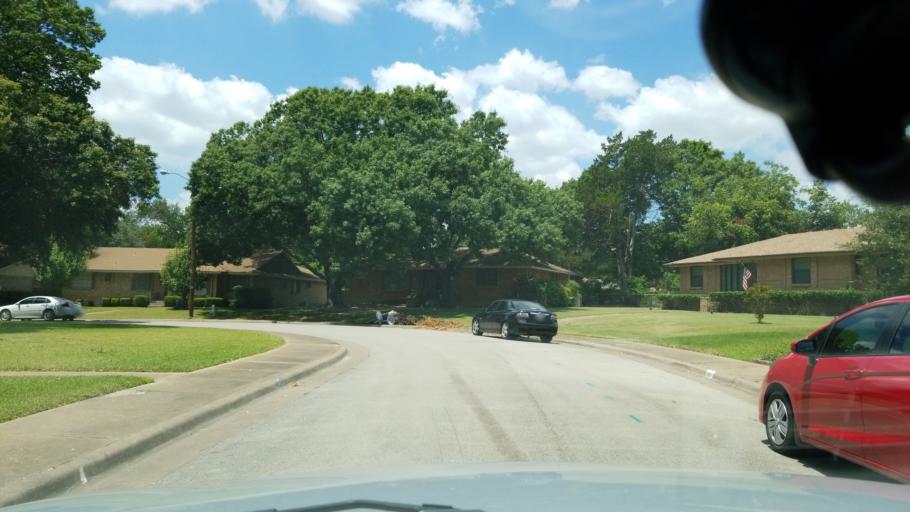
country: US
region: Texas
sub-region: Dallas County
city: Cockrell Hill
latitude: 32.6937
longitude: -96.8773
